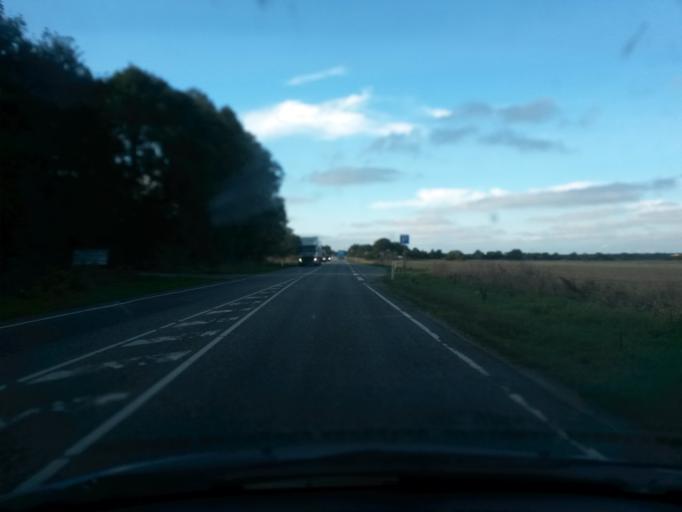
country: DK
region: Central Jutland
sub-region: Holstebro Kommune
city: Holstebro
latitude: 56.3228
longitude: 8.6724
